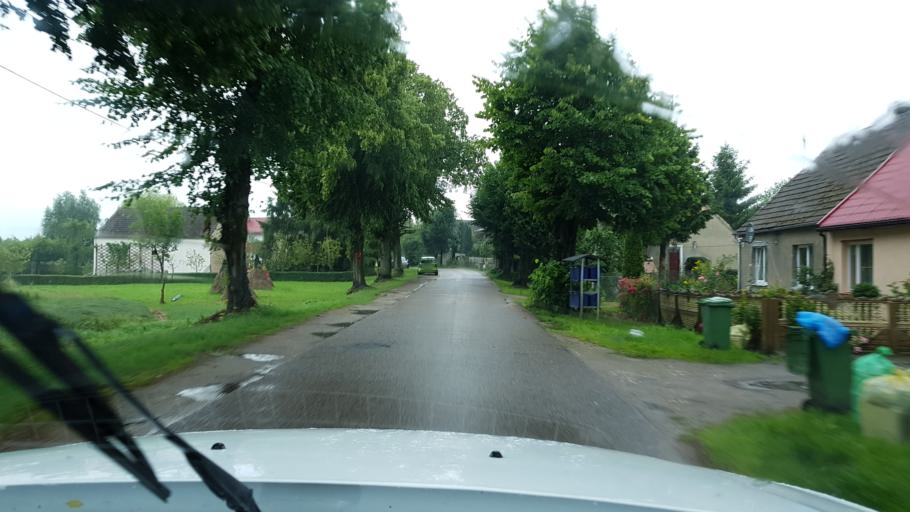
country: PL
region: West Pomeranian Voivodeship
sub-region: Powiat kolobrzeski
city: Ustronie Morskie
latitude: 54.2130
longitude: 15.8897
